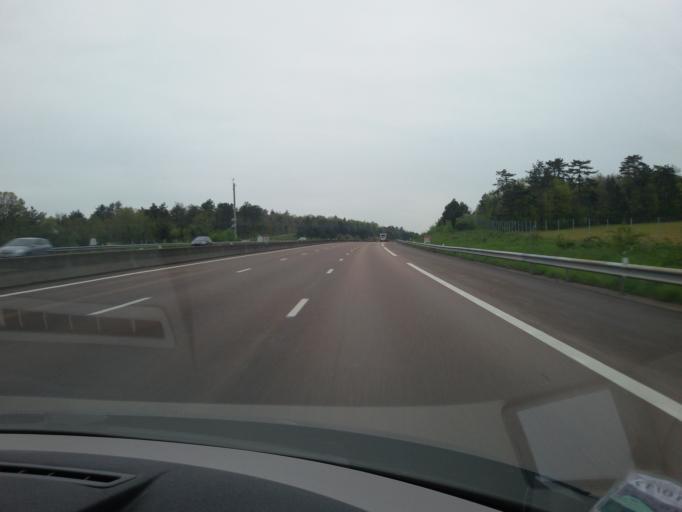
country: FR
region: Bourgogne
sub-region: Departement de la Cote-d'Or
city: Selongey
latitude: 47.5567
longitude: 5.1980
